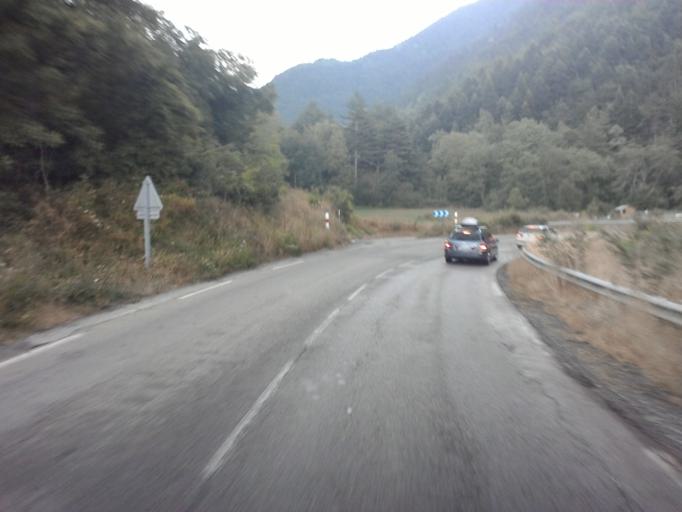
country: FR
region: Rhone-Alpes
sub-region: Departement de l'Isere
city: La Mure
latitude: 44.8231
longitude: 5.9518
